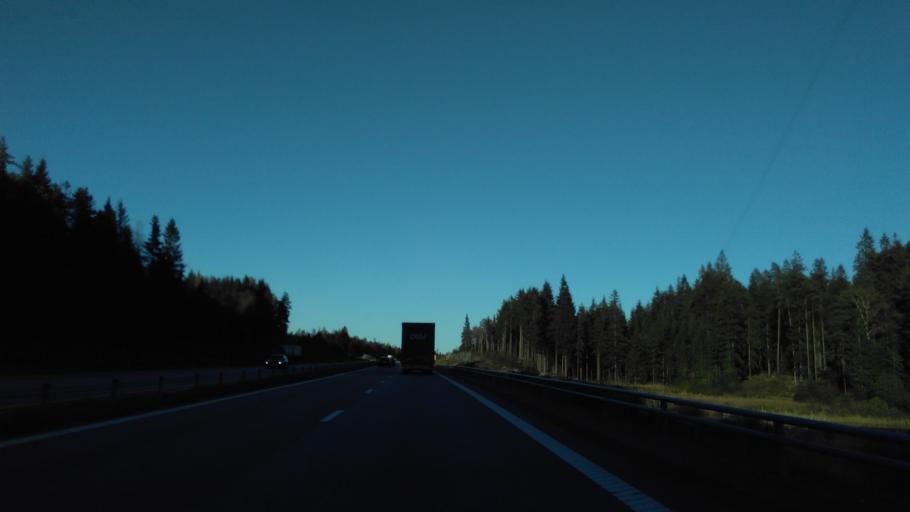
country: SE
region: Vaestra Goetaland
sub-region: Boras Kommun
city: Dalsjofors
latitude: 57.7458
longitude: 13.0666
